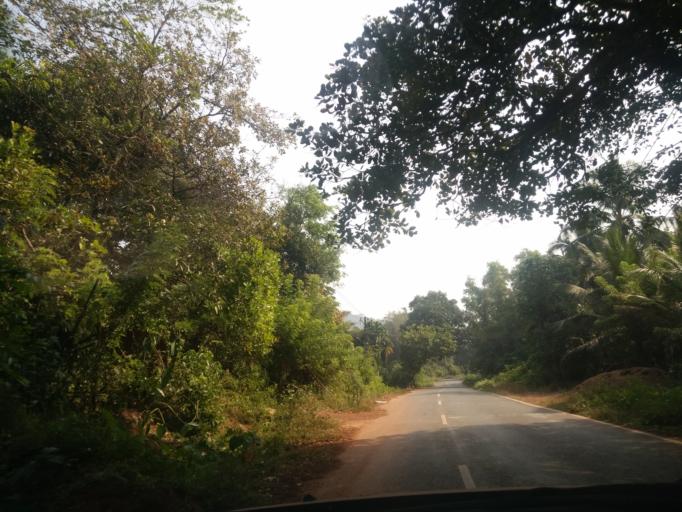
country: IN
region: Goa
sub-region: North Goa
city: Valpoy
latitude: 15.4823
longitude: 74.1342
